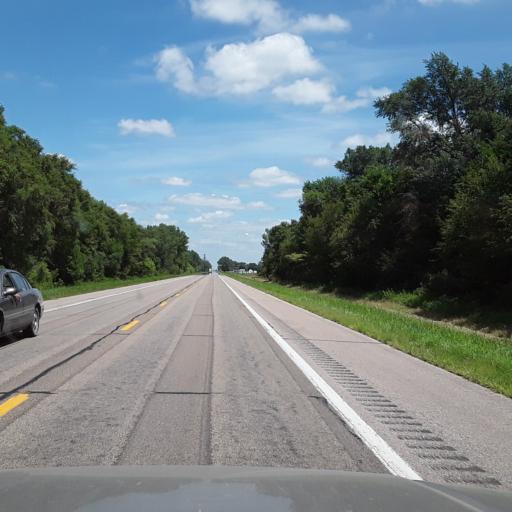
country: US
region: Nebraska
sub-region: Platte County
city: Columbus
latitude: 41.3797
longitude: -97.5137
